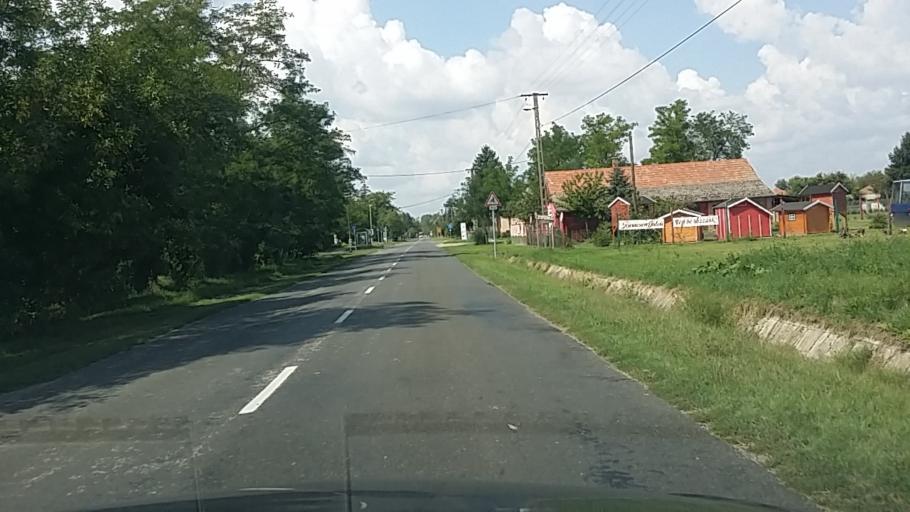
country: HU
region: Bacs-Kiskun
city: Tiszaalpar
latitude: 46.7498
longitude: 20.0396
